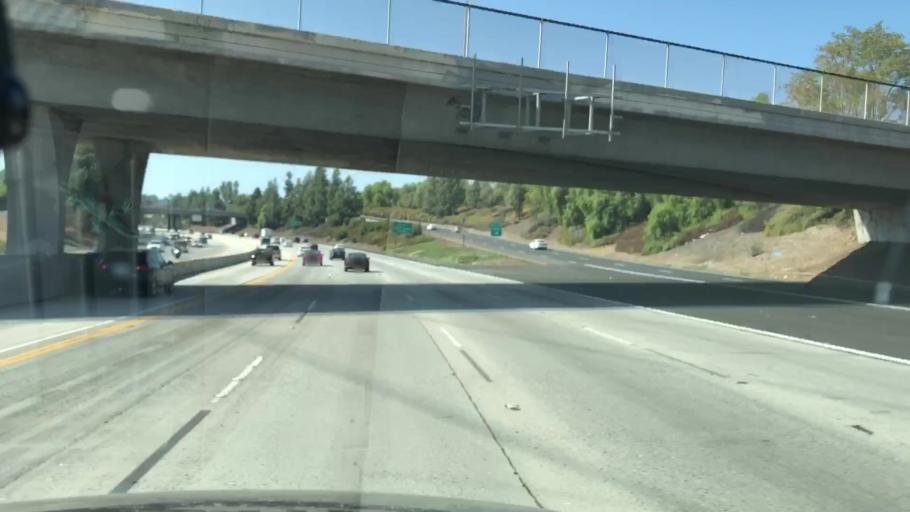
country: US
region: California
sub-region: Los Angeles County
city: San Fernando
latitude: 34.2774
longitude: -118.4976
